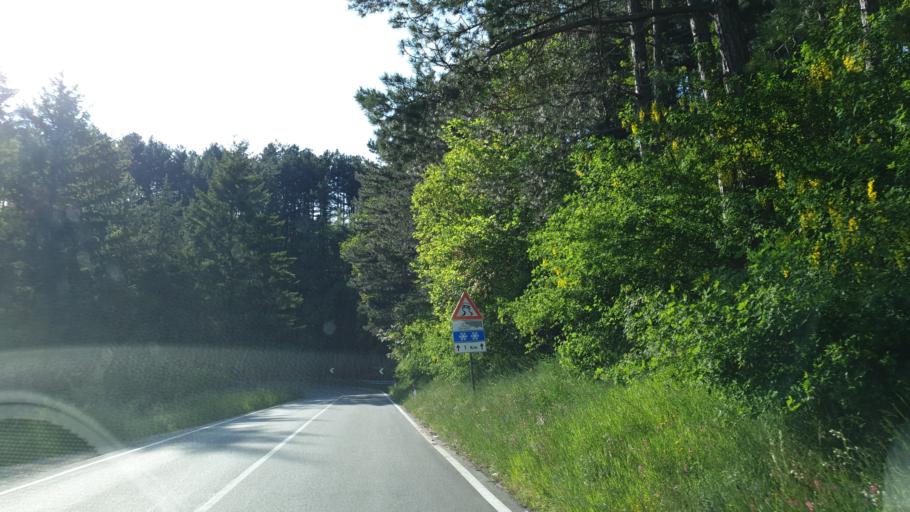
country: IT
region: Tuscany
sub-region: Province of Arezzo
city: Montemignaio
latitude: 43.7851
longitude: 11.6056
